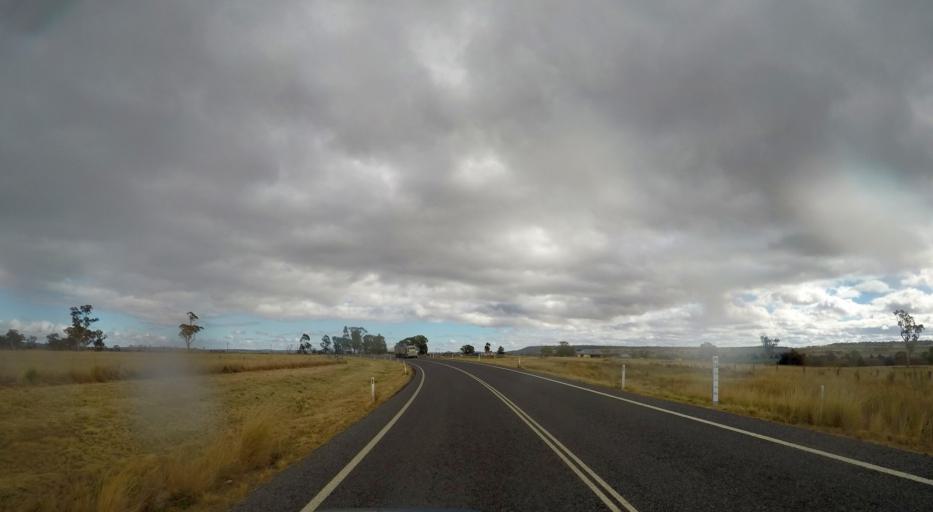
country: AU
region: Queensland
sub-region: Southern Downs
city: Warwick
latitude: -28.0448
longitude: 152.0481
